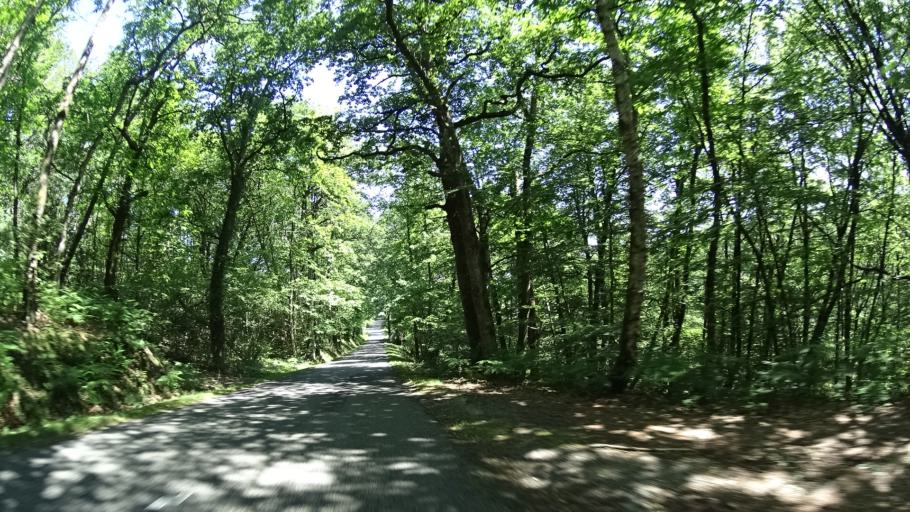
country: FR
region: Brittany
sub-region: Departement d'Ille-et-Vilaine
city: Langon
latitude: 47.7668
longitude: -1.8486
